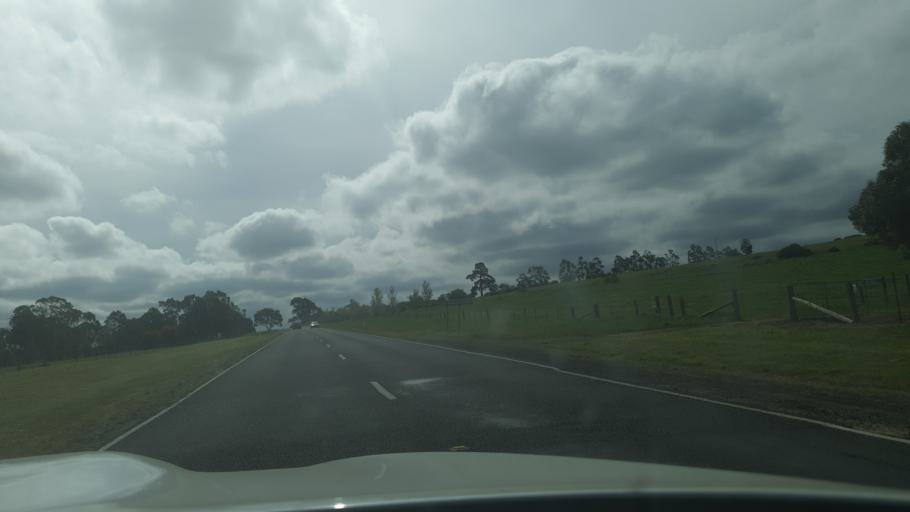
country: AU
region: Victoria
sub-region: Central Goldfields
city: Maryborough
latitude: -37.2106
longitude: 143.7217
